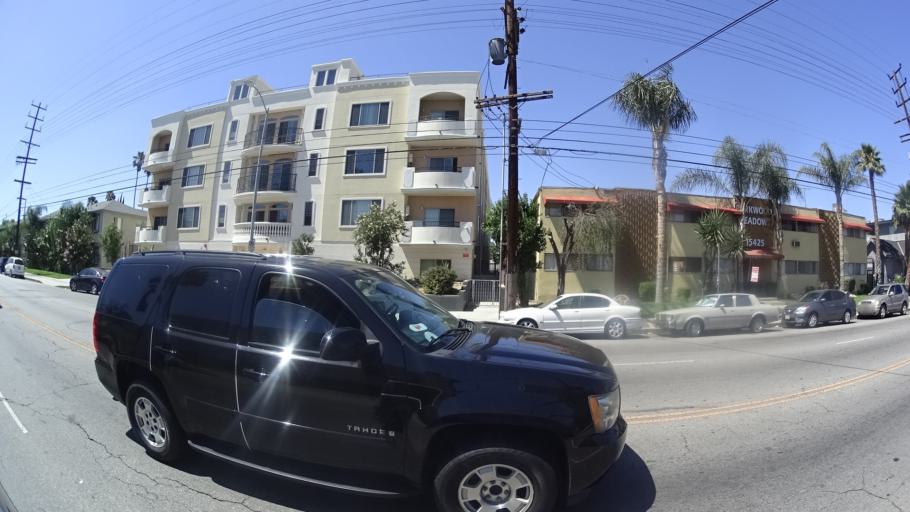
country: US
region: California
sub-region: Los Angeles County
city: Van Nuys
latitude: 34.1939
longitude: -118.4696
